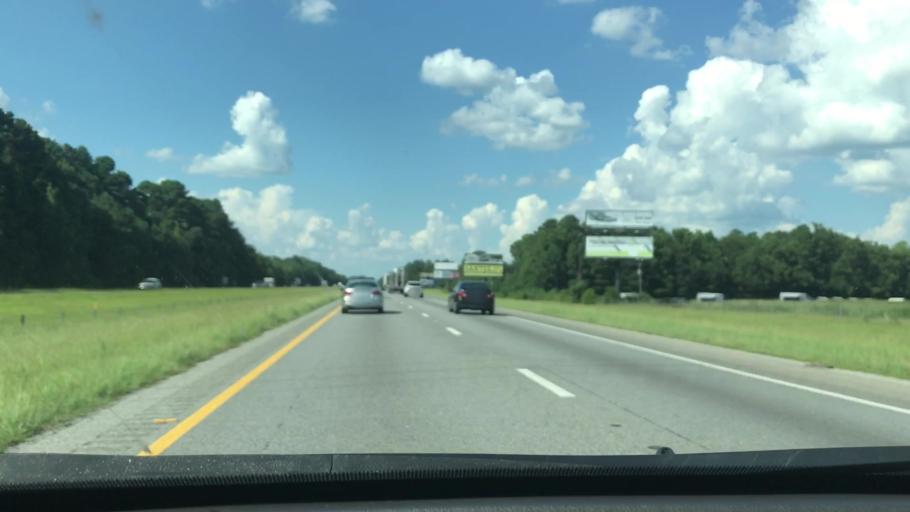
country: US
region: South Carolina
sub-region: Orangeburg County
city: Holly Hill
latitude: 33.4252
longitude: -80.4906
